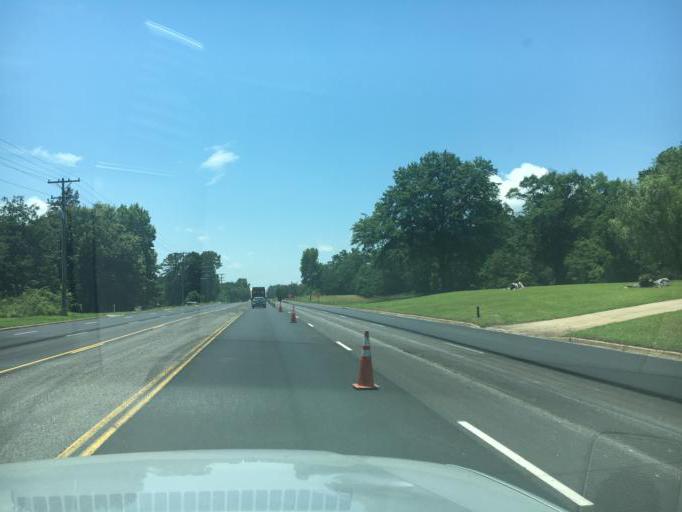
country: US
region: South Carolina
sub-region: Greenville County
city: Travelers Rest
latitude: 34.9430
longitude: -82.4416
